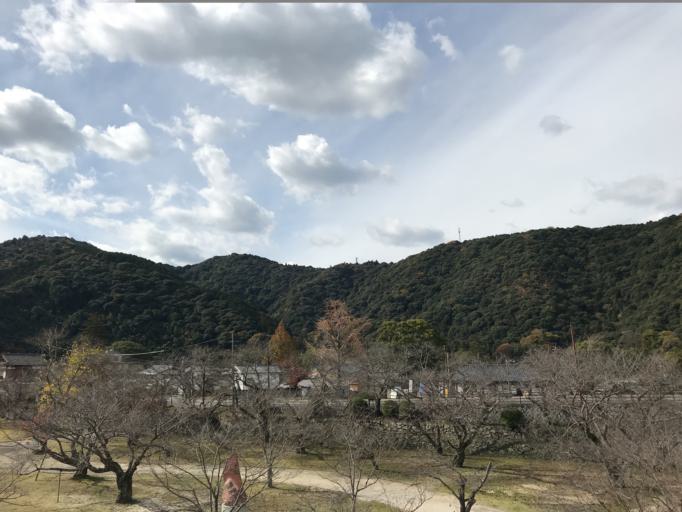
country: JP
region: Yamaguchi
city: Iwakuni
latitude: 34.1697
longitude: 132.1791
